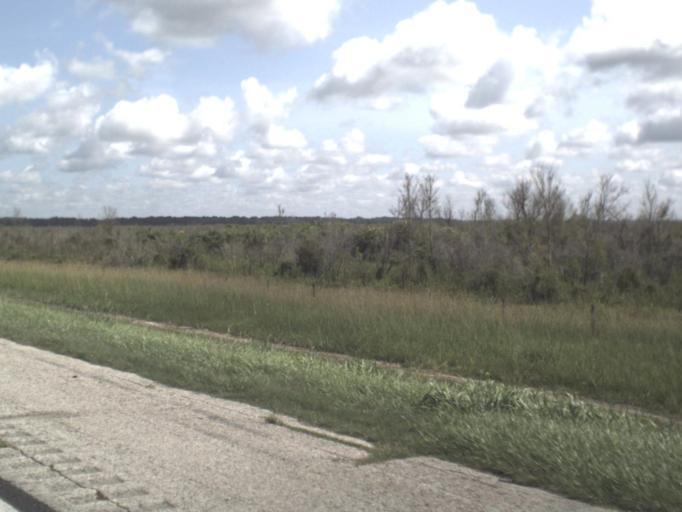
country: US
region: Florida
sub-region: Alachua County
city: Gainesville
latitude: 29.5621
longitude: -82.3464
